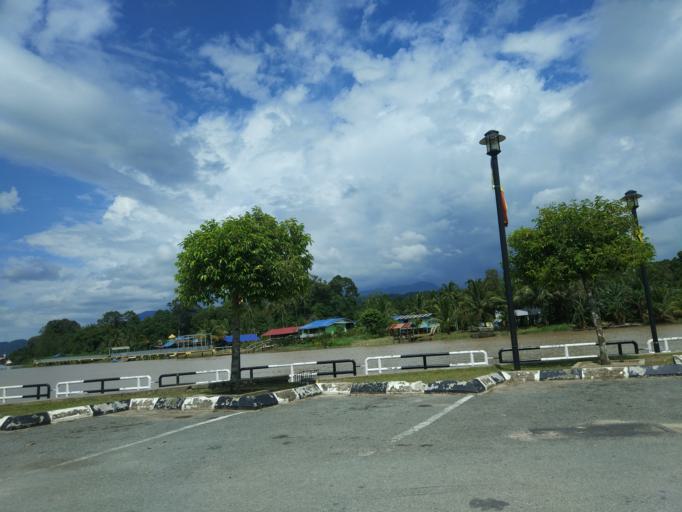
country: BN
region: Temburong
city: Bangar
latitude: 4.8578
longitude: 115.4080
